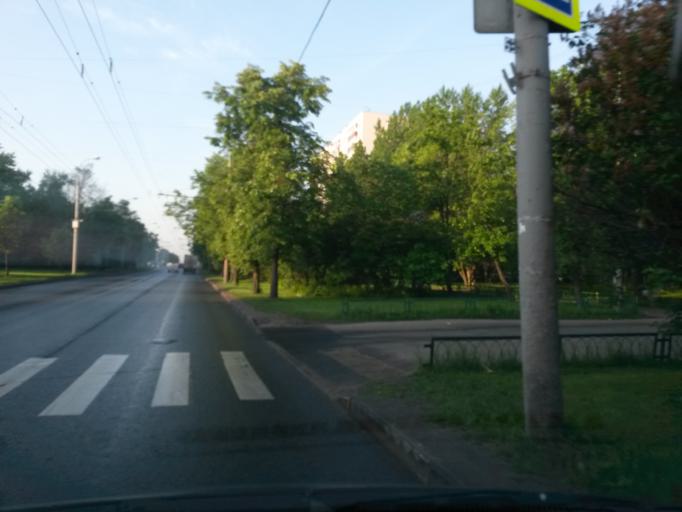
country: RU
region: Moscow
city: Metrogorodok
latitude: 55.8190
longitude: 37.7981
